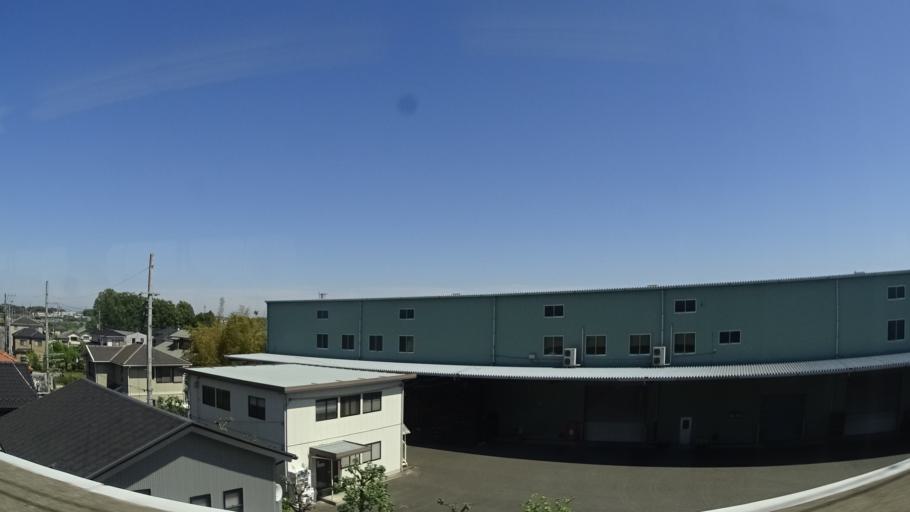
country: JP
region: Saitama
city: Ageoshimo
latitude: 35.9913
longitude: 139.6326
